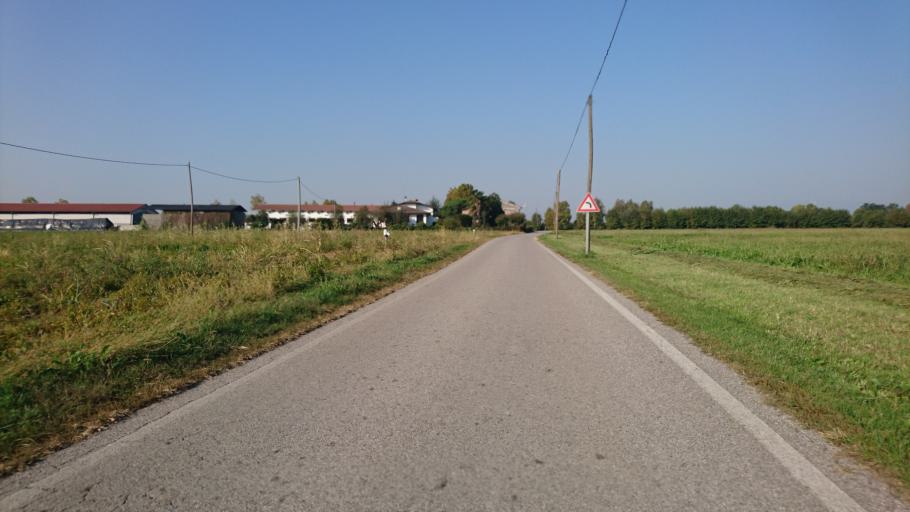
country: IT
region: Veneto
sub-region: Provincia di Padova
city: Gazzo
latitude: 45.6019
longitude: 11.7085
